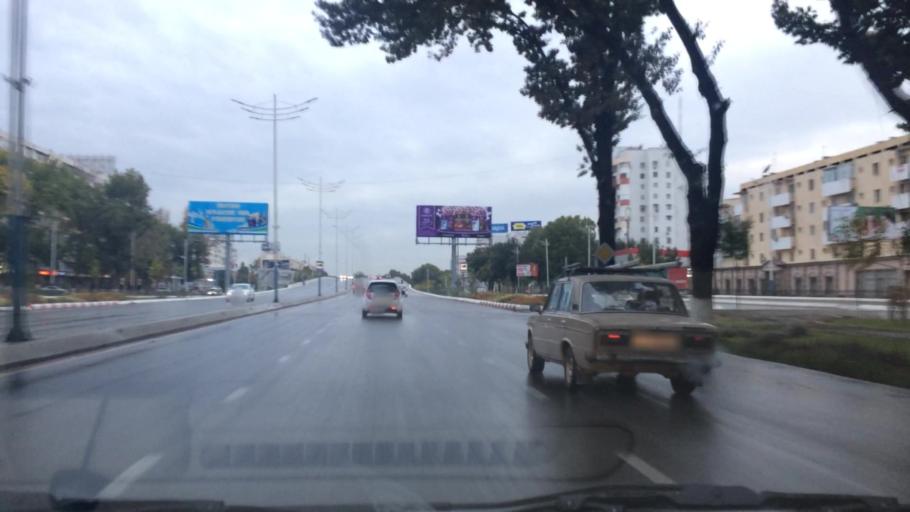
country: UZ
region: Toshkent Shahri
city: Tashkent
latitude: 41.2949
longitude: 69.2265
